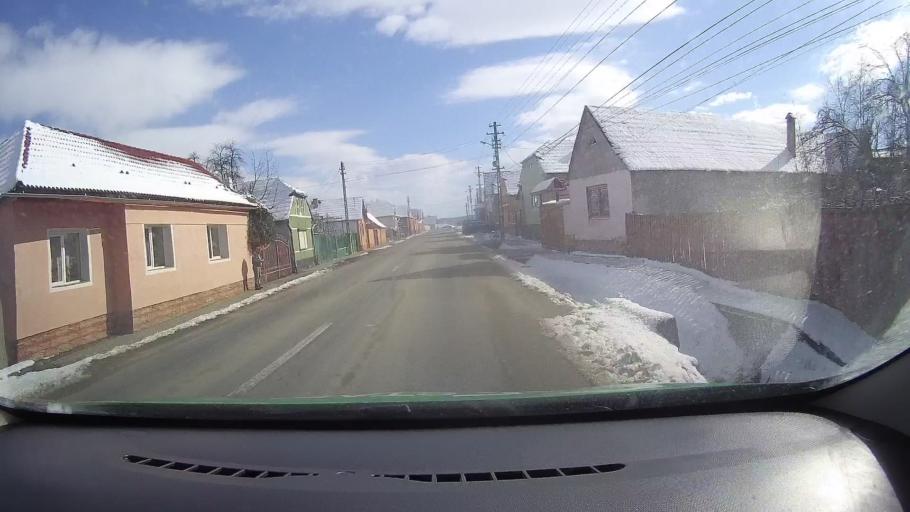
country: RO
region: Sibiu
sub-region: Comuna Barghis
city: Barghis
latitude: 45.9806
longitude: 24.5395
